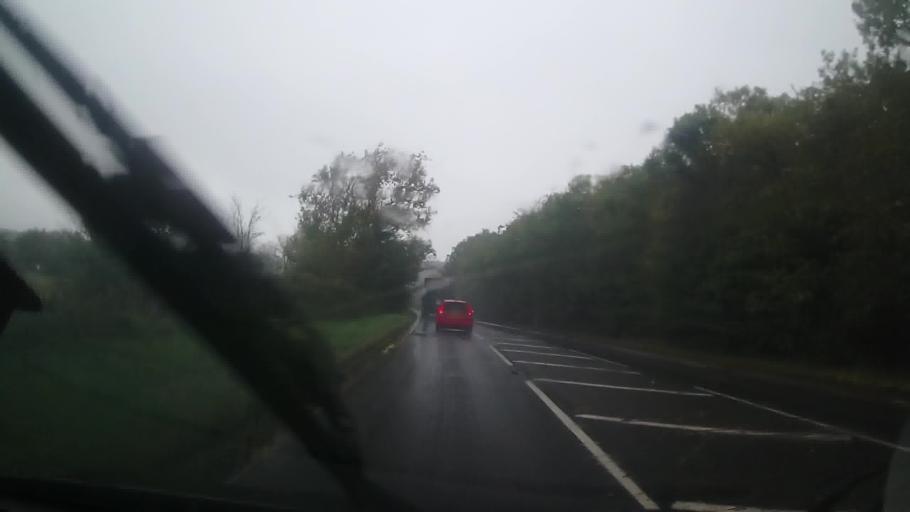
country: GB
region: England
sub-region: Worcestershire
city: Evesham
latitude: 52.1212
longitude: -1.9773
